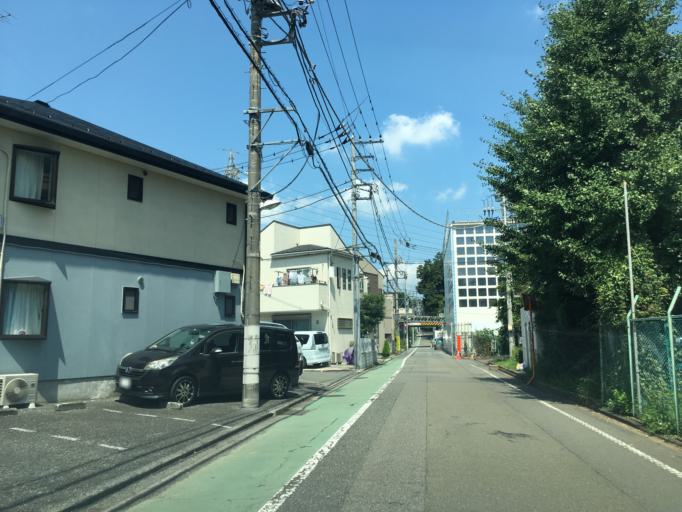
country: JP
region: Tokyo
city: Fussa
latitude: 35.7186
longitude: 139.3510
